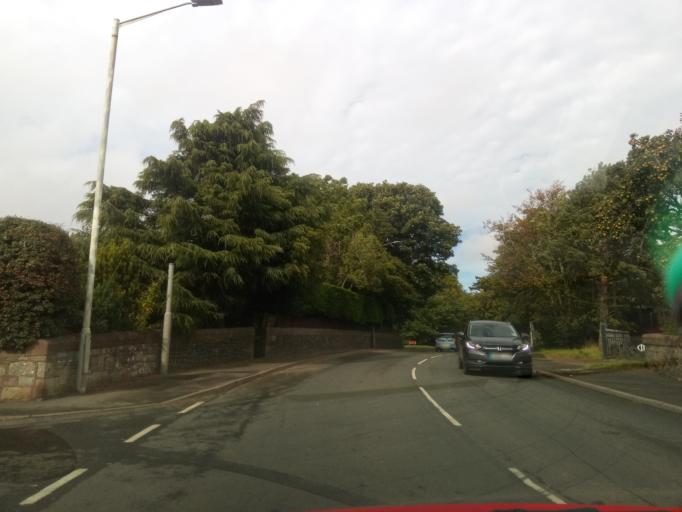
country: GB
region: Scotland
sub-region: The Scottish Borders
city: Duns
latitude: 55.7726
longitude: -2.3403
